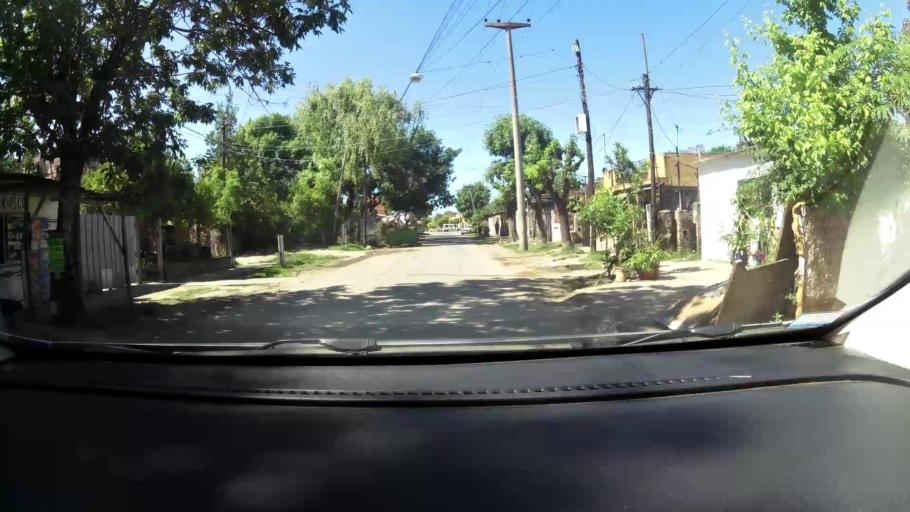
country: AR
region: Santa Fe
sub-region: Departamento de Rosario
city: Rosario
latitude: -32.9735
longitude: -60.6925
